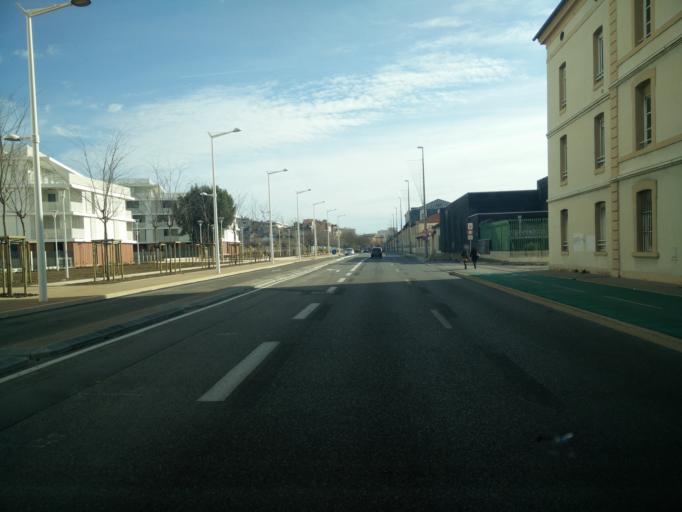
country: FR
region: Provence-Alpes-Cote d'Azur
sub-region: Departement du Var
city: Toulon
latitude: 43.1260
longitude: 5.9227
